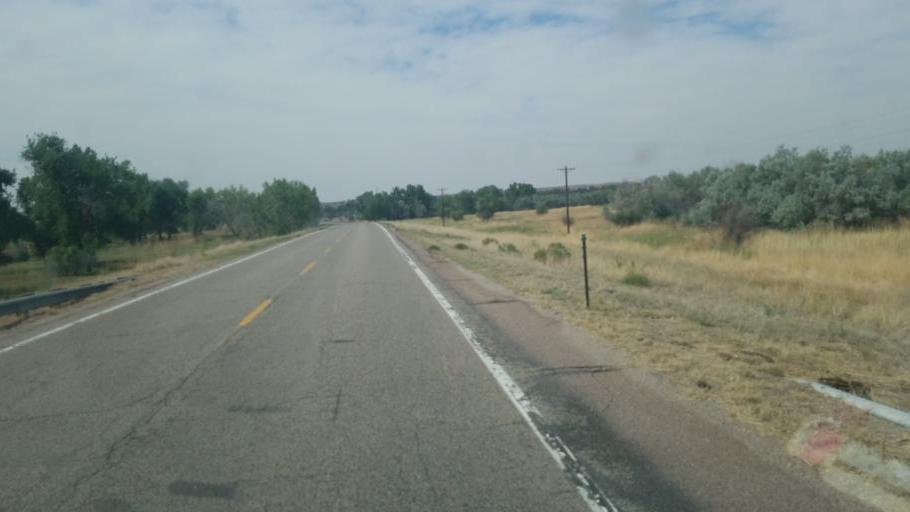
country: US
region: Colorado
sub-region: Otero County
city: Fowler
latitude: 38.2342
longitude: -104.2613
